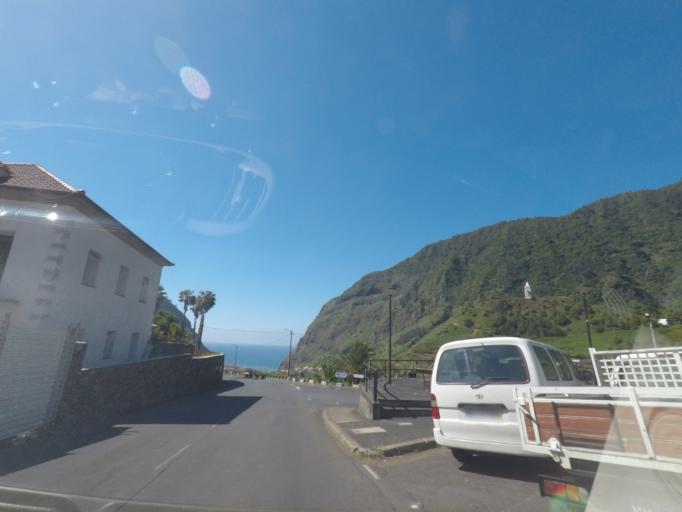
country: PT
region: Madeira
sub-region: Sao Vicente
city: Sao Vicente
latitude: 32.7925
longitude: -17.0386
